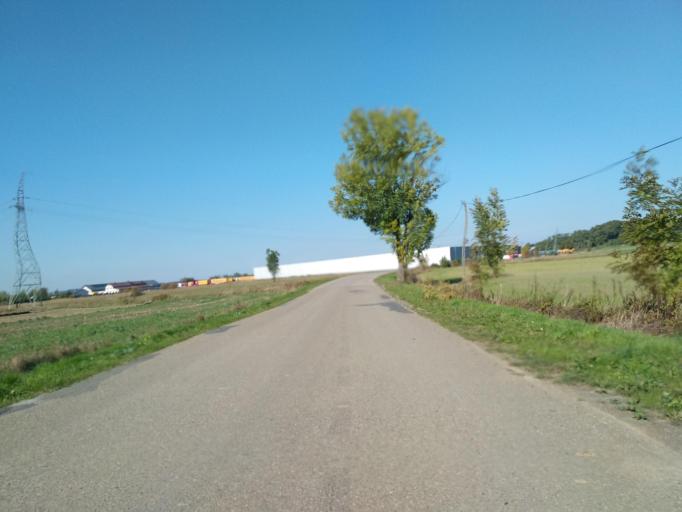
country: PL
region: Subcarpathian Voivodeship
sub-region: Powiat debicki
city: Pilzno
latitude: 49.9808
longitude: 21.3241
